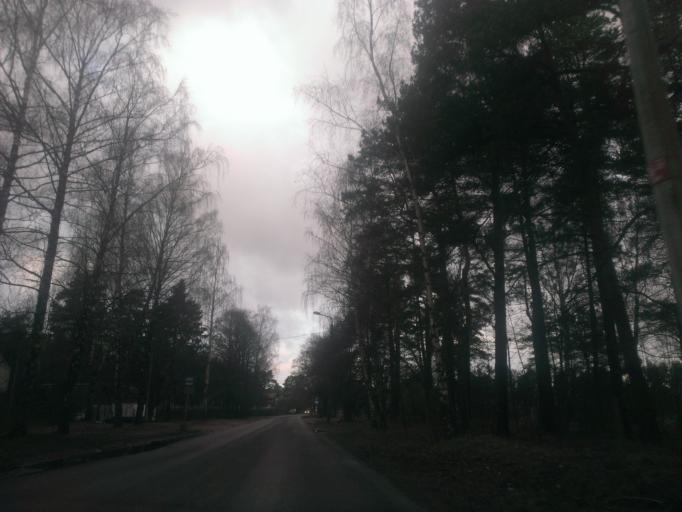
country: LV
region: Riga
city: Bergi
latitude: 56.9947
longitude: 24.2824
